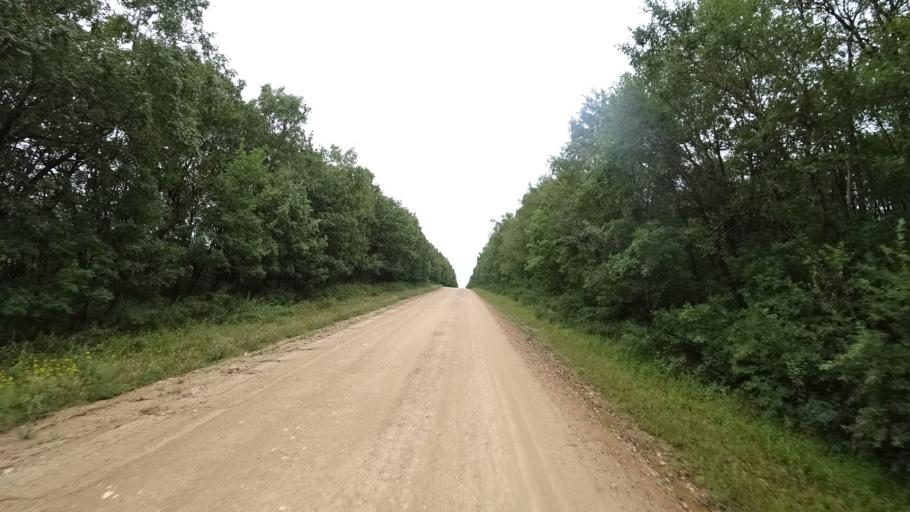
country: RU
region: Primorskiy
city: Ivanovka
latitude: 44.0306
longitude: 132.5296
